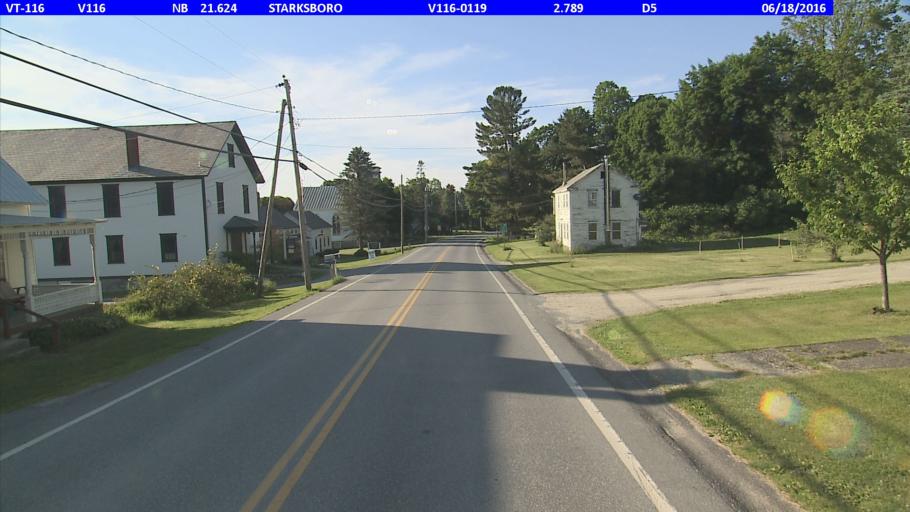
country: US
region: Vermont
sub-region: Addison County
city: Bristol
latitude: 44.2248
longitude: -73.0569
